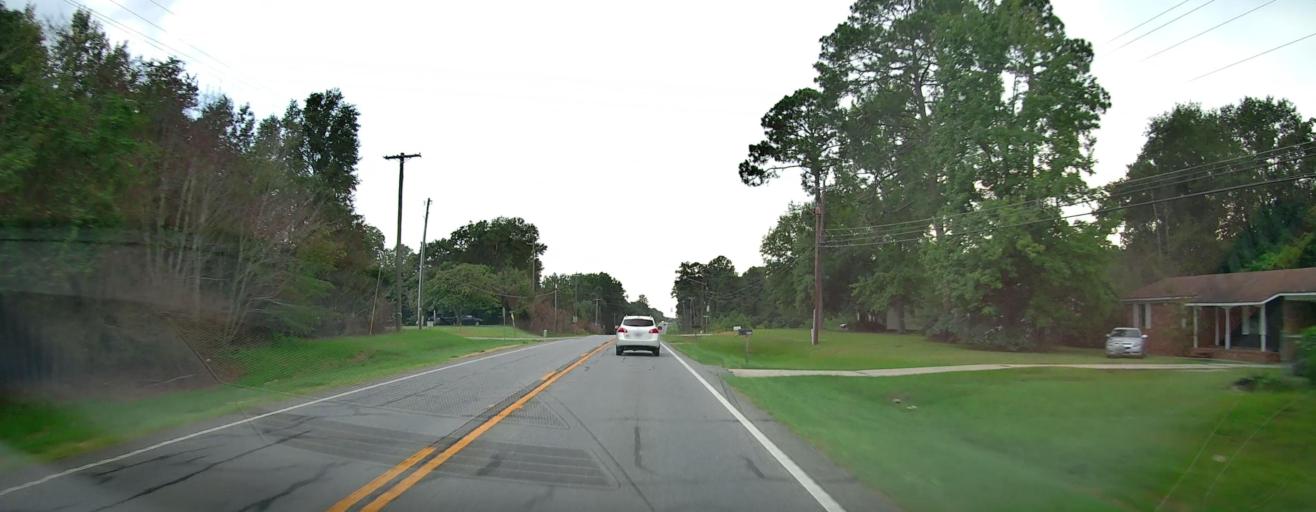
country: US
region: Georgia
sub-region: Laurens County
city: East Dublin
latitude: 32.5591
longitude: -82.8561
